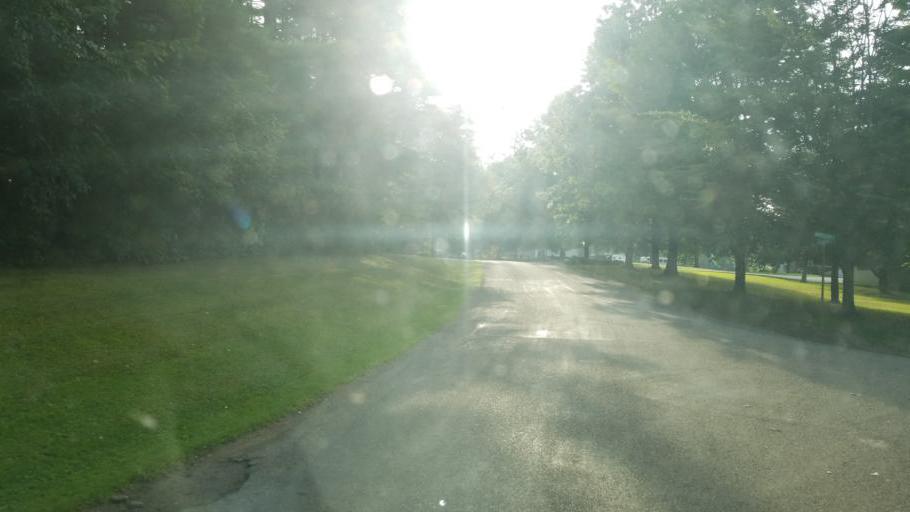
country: US
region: Ohio
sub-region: Sandusky County
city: Bellville
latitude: 40.6435
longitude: -82.4934
